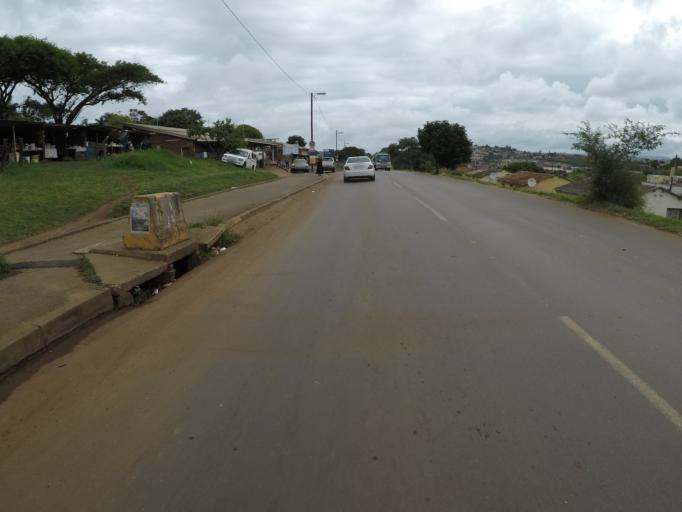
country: ZA
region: KwaZulu-Natal
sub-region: uThungulu District Municipality
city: Empangeni
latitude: -28.7772
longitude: 31.8647
